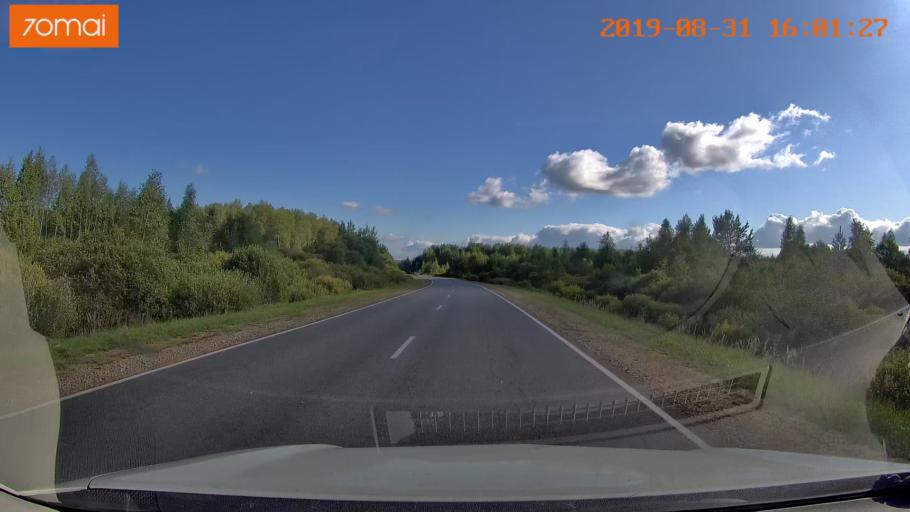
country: RU
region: Kaluga
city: Yukhnov
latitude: 54.6893
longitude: 35.2901
